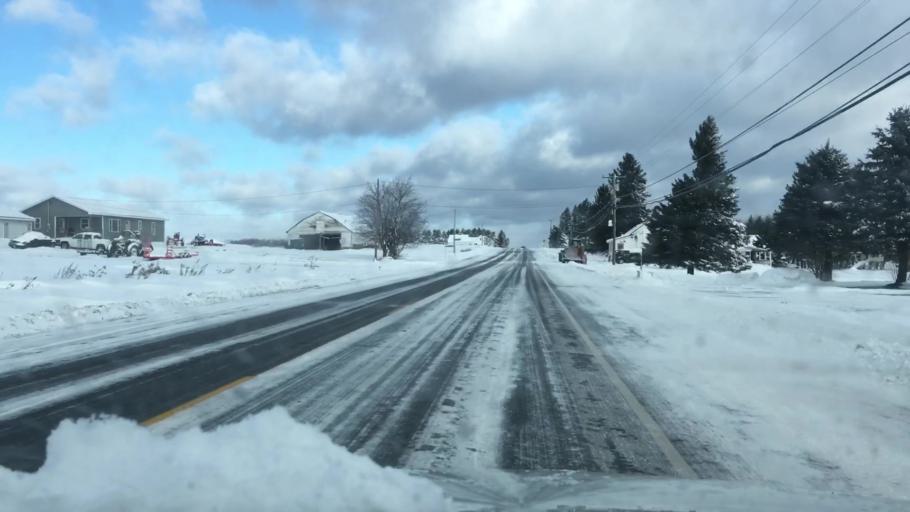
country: US
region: Maine
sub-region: Aroostook County
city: Caribou
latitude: 46.9078
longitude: -68.0165
